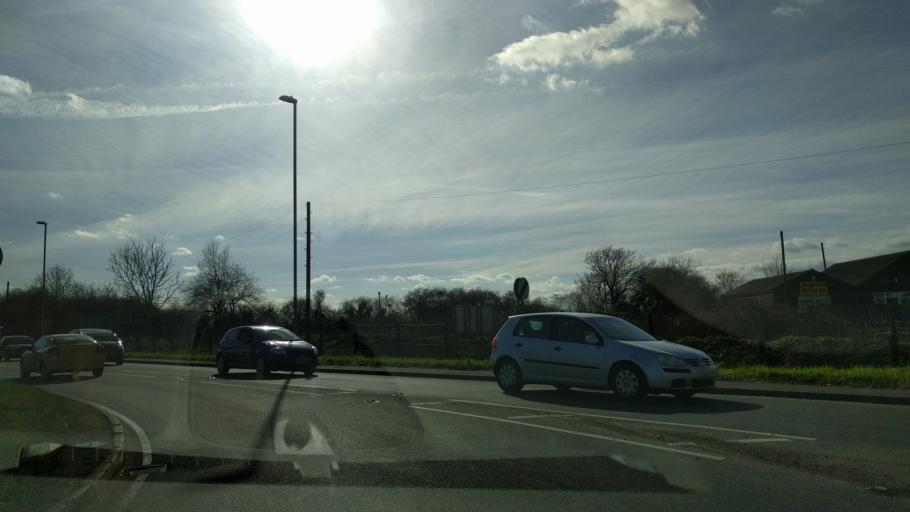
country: GB
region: England
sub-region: Cambridgeshire
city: Chatteris
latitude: 52.4647
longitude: 0.0436
